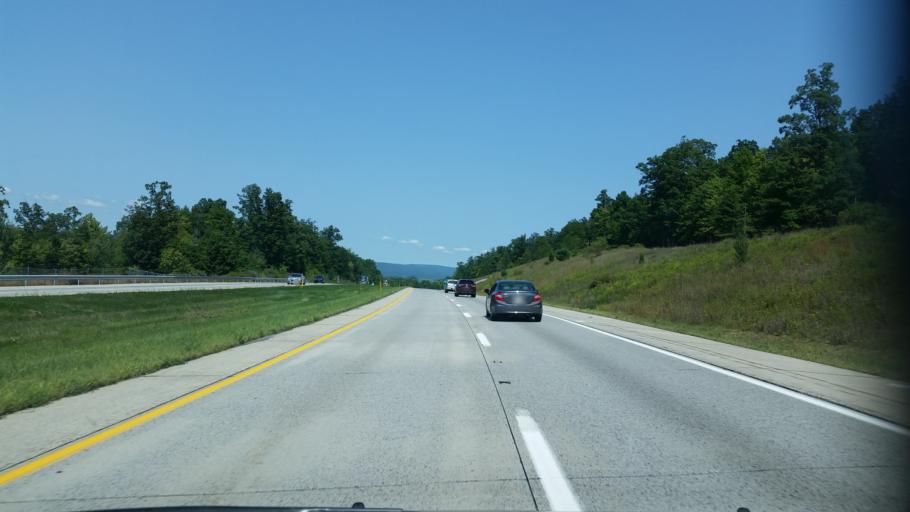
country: US
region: Pennsylvania
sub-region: Blair County
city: Greenwood
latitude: 40.5281
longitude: -78.3519
